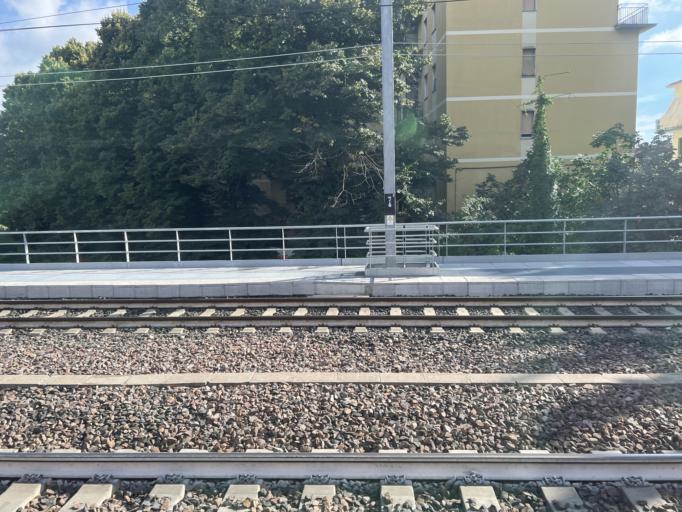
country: IT
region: Emilia-Romagna
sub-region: Provincia di Parma
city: Parma
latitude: 44.8110
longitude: 10.3246
